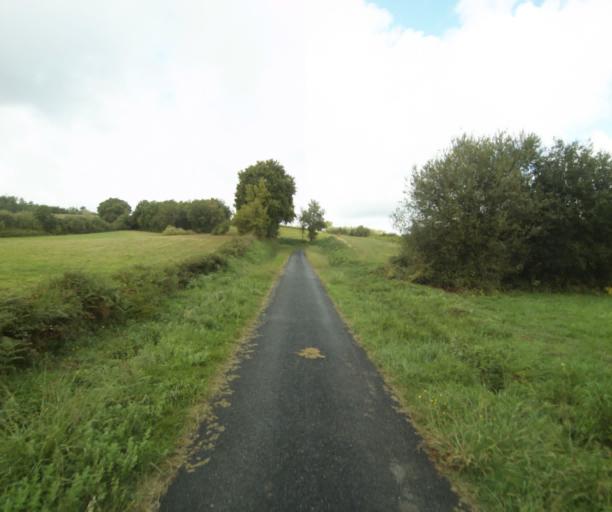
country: FR
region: Midi-Pyrenees
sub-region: Departement du Gers
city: Nogaro
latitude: 43.8261
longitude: -0.0905
